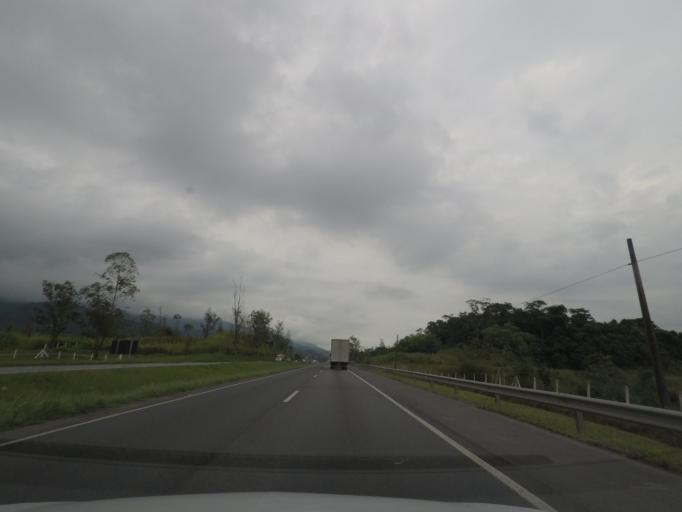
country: BR
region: Sao Paulo
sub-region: Miracatu
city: Miracatu
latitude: -24.2694
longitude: -47.3986
